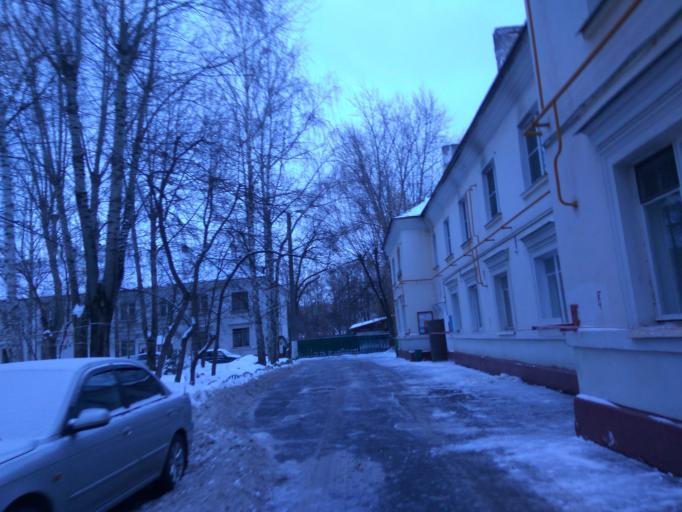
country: RU
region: Moskovskaya
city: Kur'yanovo
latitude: 55.6537
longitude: 37.7034
